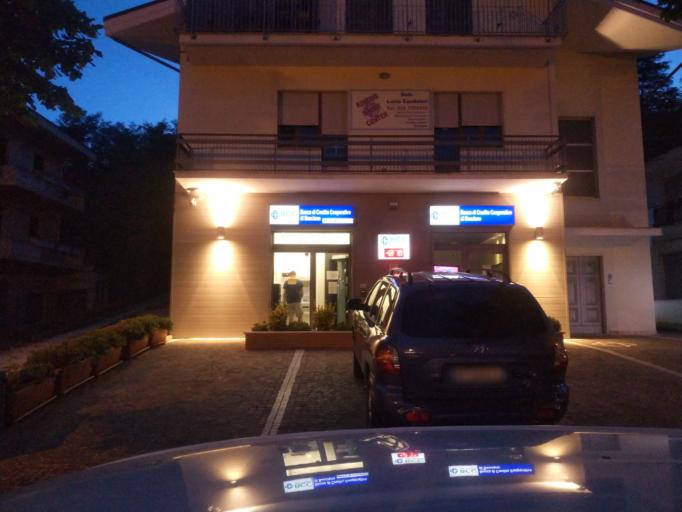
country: IT
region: Abruzzo
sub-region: Provincia di Teramo
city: Isola del Gran Sasso d'Italia
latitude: 42.5131
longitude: 13.6571
